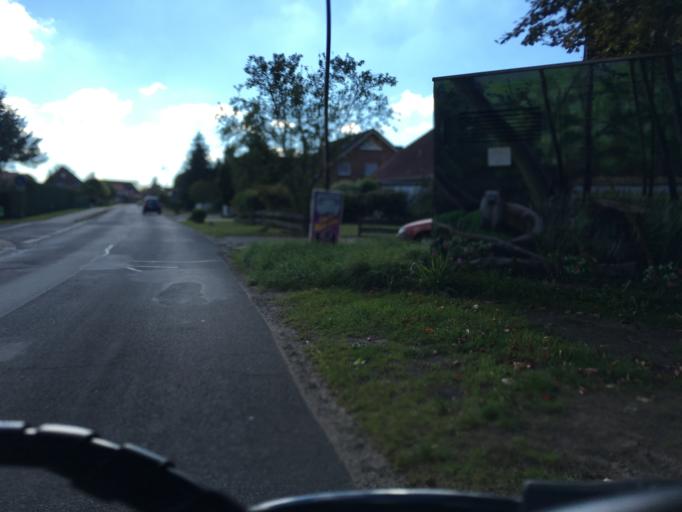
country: DE
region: Lower Saxony
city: Bardowick
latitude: 53.3080
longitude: 10.3869
